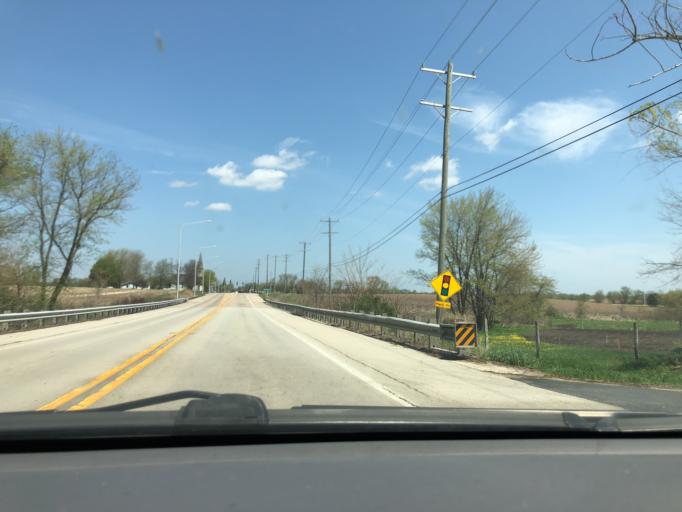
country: US
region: Illinois
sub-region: Kane County
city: Pingree Grove
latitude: 42.0517
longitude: -88.4642
